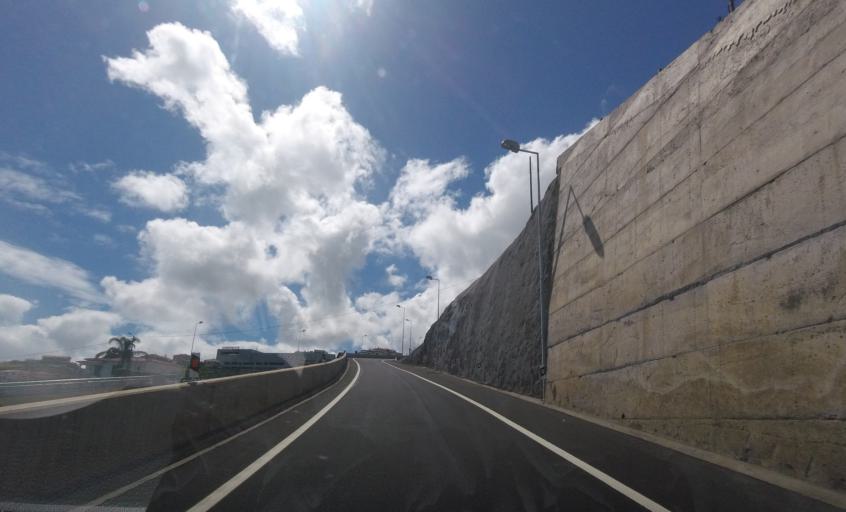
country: PT
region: Madeira
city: Camara de Lobos
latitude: 32.6704
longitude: -16.9731
